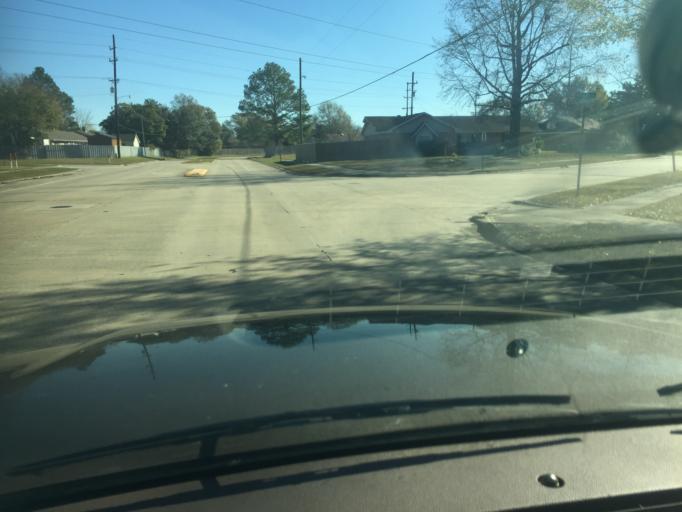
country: US
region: Louisiana
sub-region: Saint Tammany Parish
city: Slidell
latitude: 30.3017
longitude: -89.7694
